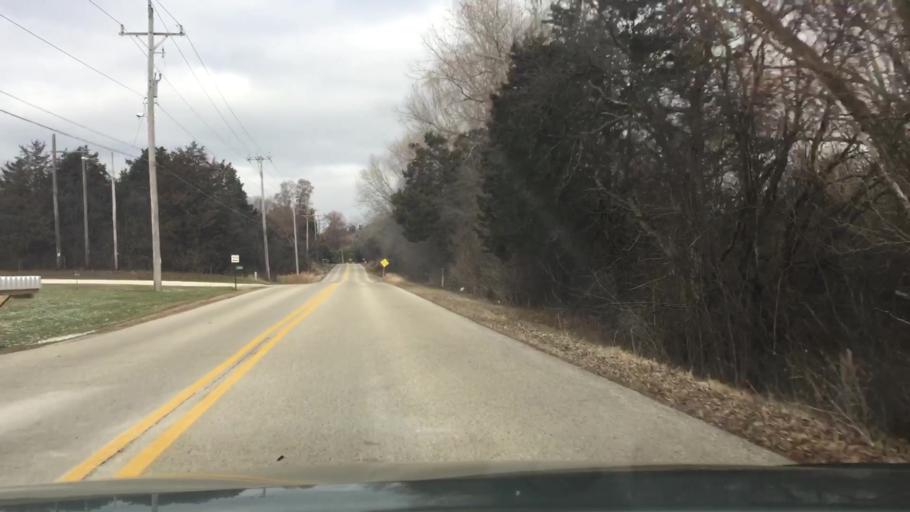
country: US
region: Wisconsin
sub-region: Waukesha County
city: Oconomowoc
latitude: 43.0732
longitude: -88.4811
